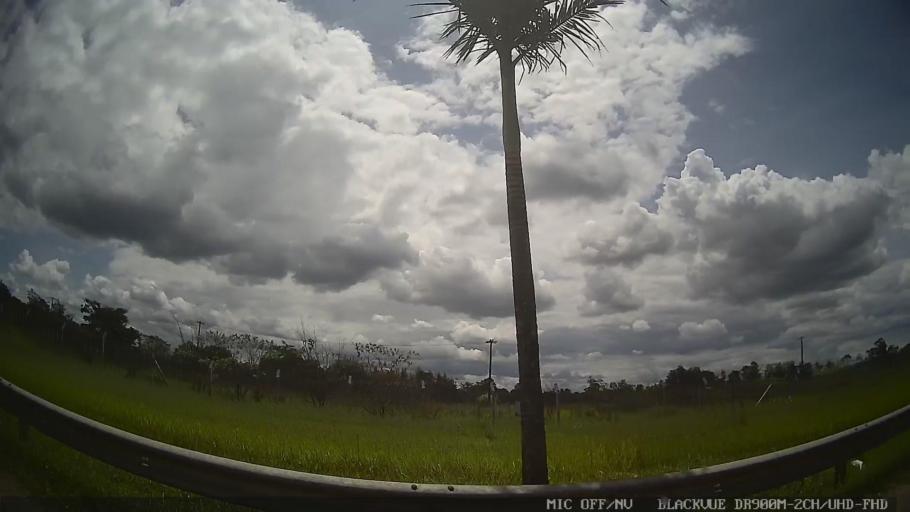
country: BR
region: Sao Paulo
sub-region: Suzano
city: Suzano
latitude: -23.5715
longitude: -46.2551
